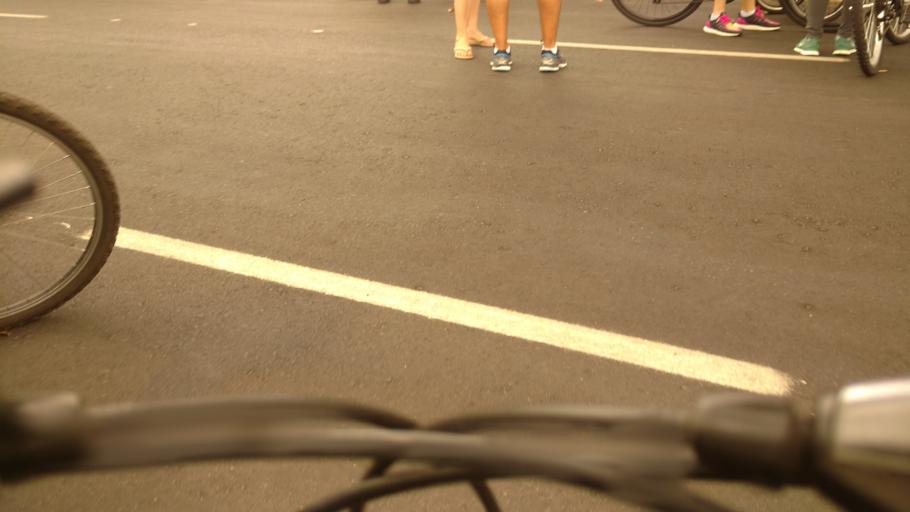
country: BR
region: Ceara
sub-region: Fortaleza
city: Fortaleza
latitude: -3.7438
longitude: -38.4861
